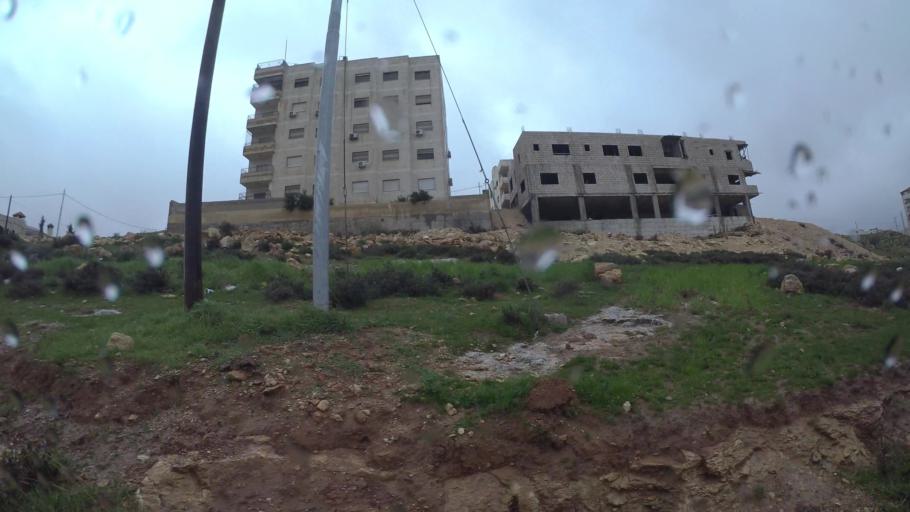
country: JO
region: Amman
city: Al Jubayhah
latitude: 32.0386
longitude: 35.8918
